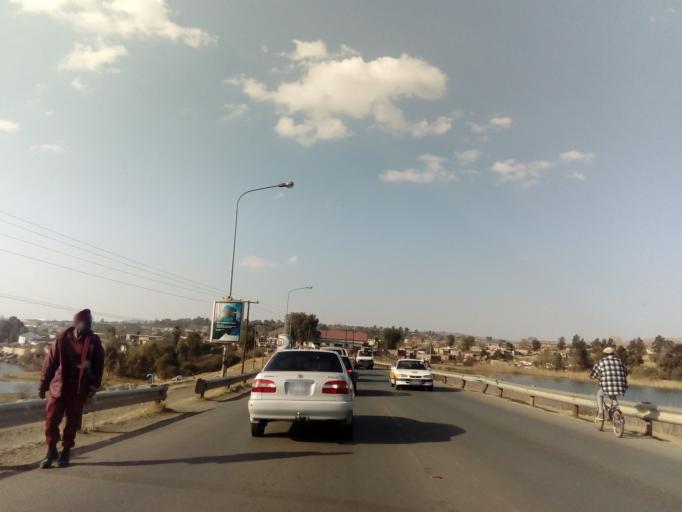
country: LS
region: Maseru
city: Maseru
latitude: -29.3121
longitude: 27.5108
